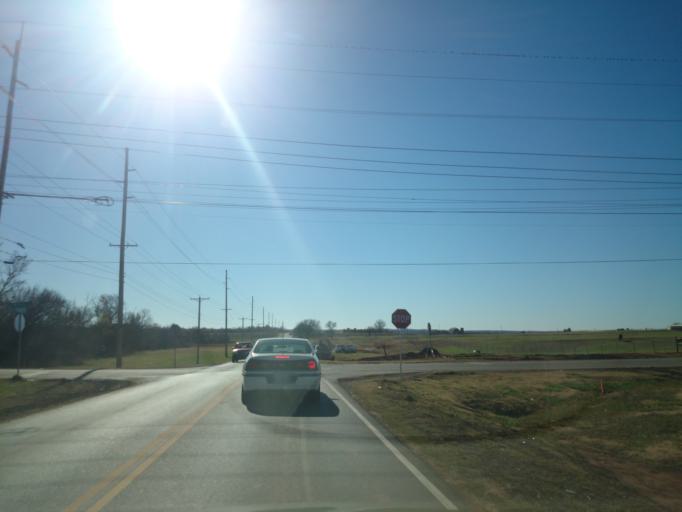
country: US
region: Oklahoma
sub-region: Payne County
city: Stillwater
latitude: 36.1307
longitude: -97.0873
